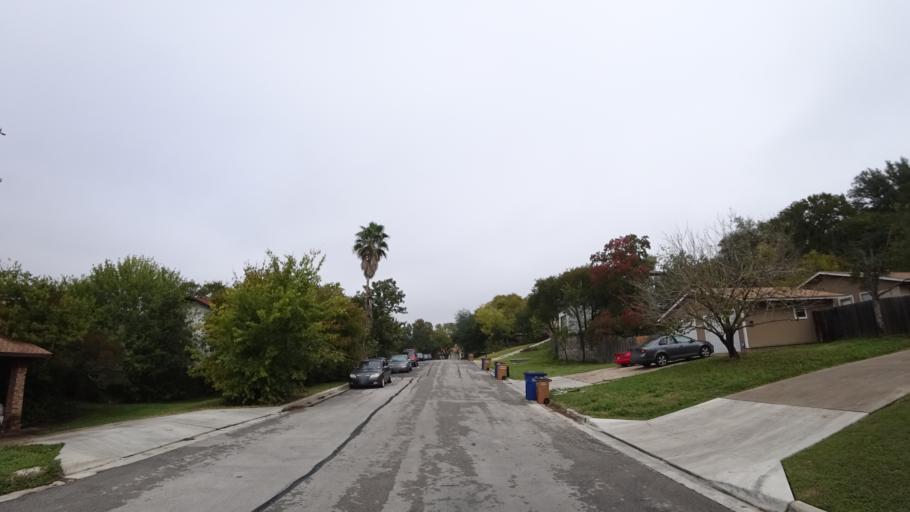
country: US
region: Texas
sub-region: Travis County
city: Rollingwood
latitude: 30.2553
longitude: -97.7797
